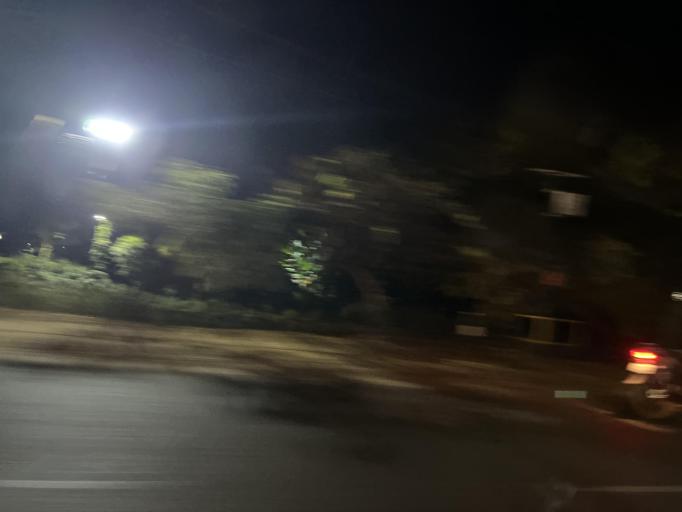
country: IN
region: Odisha
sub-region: Cuttack
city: Cuttack
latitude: 20.3714
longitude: 85.8907
